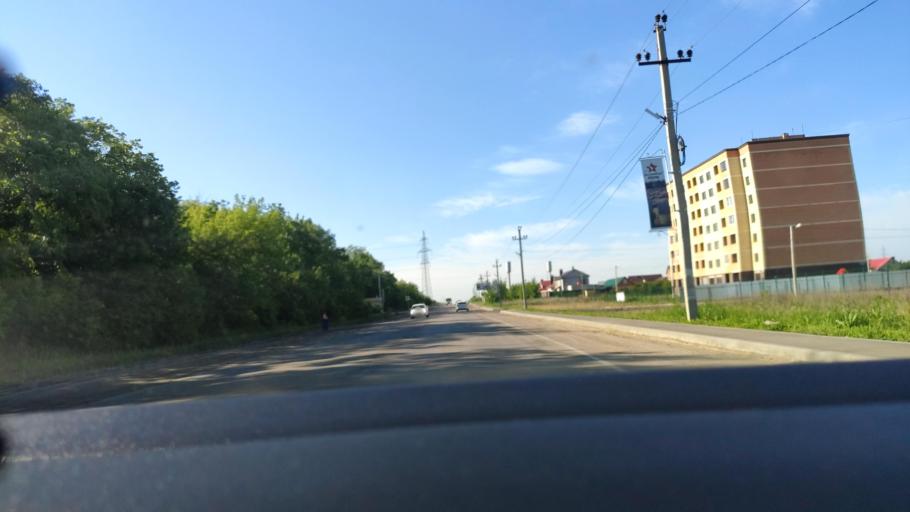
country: RU
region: Voronezj
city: Novaya Usman'
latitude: 51.6290
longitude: 39.3338
